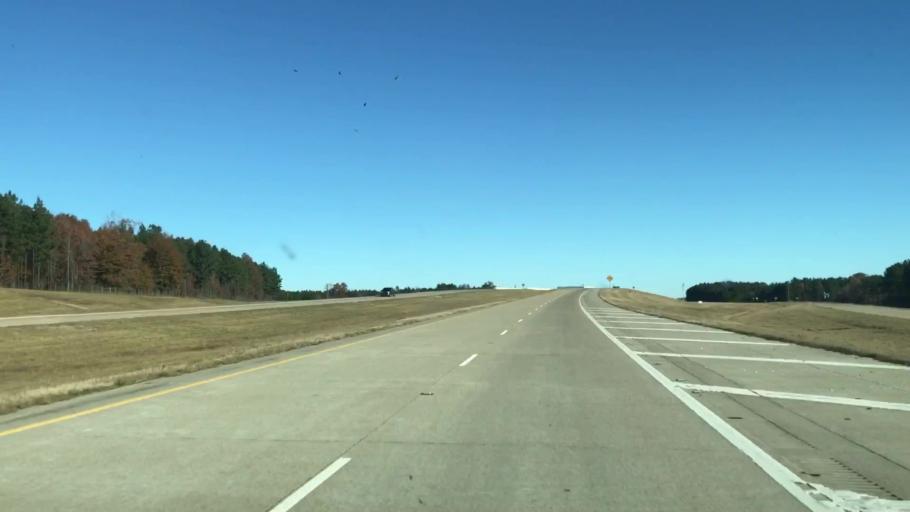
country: US
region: Louisiana
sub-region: Caddo Parish
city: Oil City
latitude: 32.8114
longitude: -93.8843
